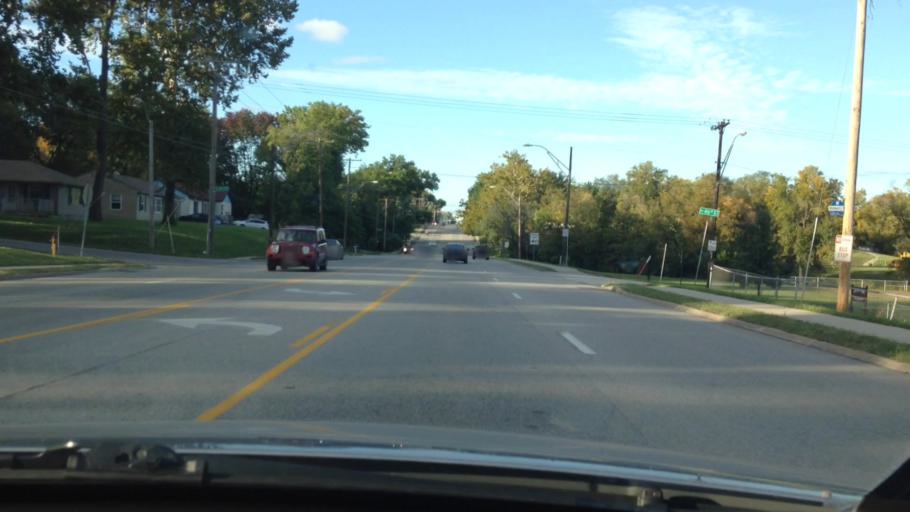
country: US
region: Missouri
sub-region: Clay County
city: Gladstone
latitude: 39.1770
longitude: -94.5490
